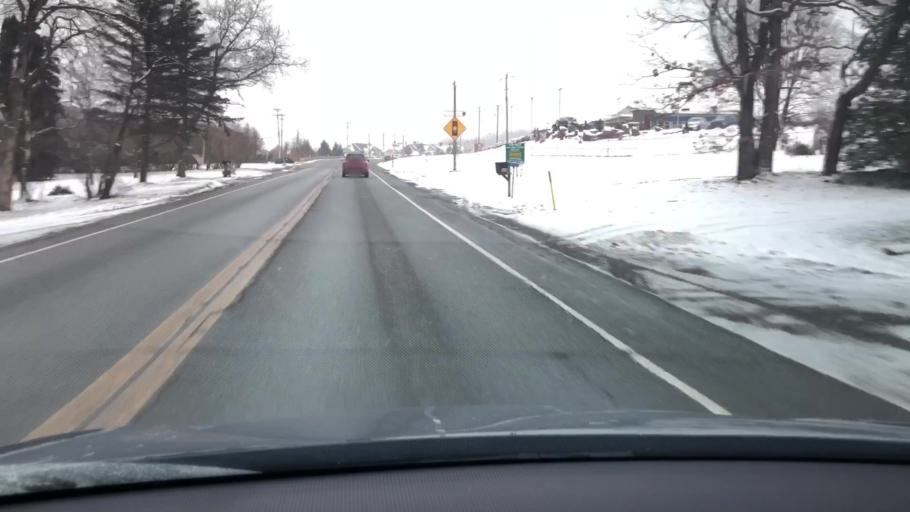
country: US
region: Pennsylvania
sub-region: Butler County
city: Seven Fields
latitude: 40.6951
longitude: -80.0430
